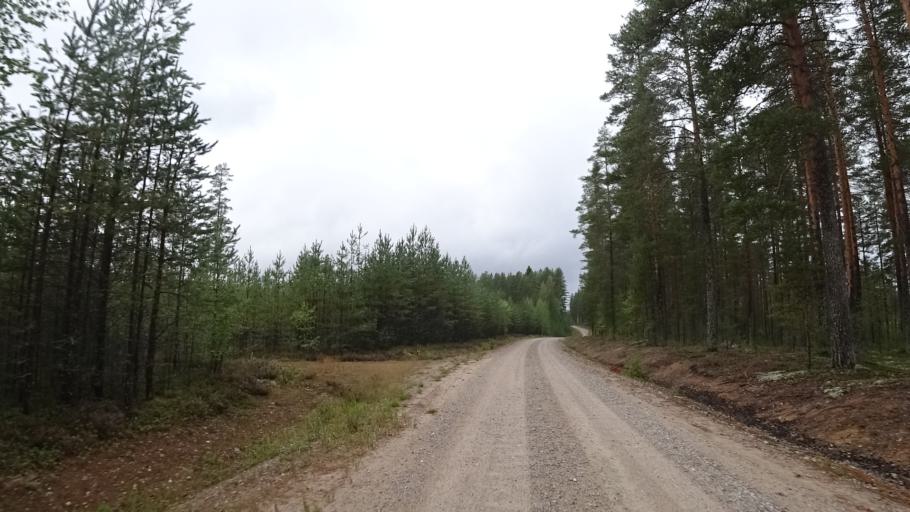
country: FI
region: North Karelia
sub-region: Pielisen Karjala
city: Lieksa
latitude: 63.5295
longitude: 30.0682
